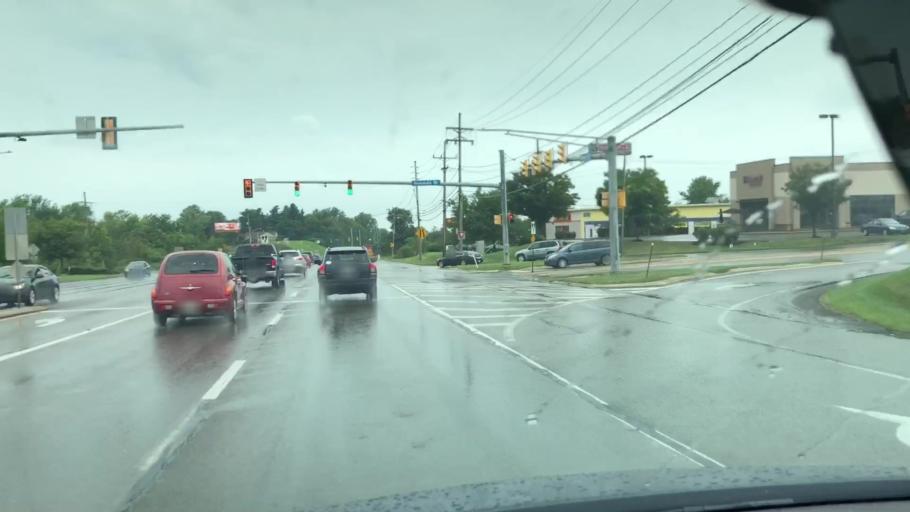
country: US
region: Pennsylvania
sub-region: Erie County
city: Erie
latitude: 42.0572
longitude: -80.0900
